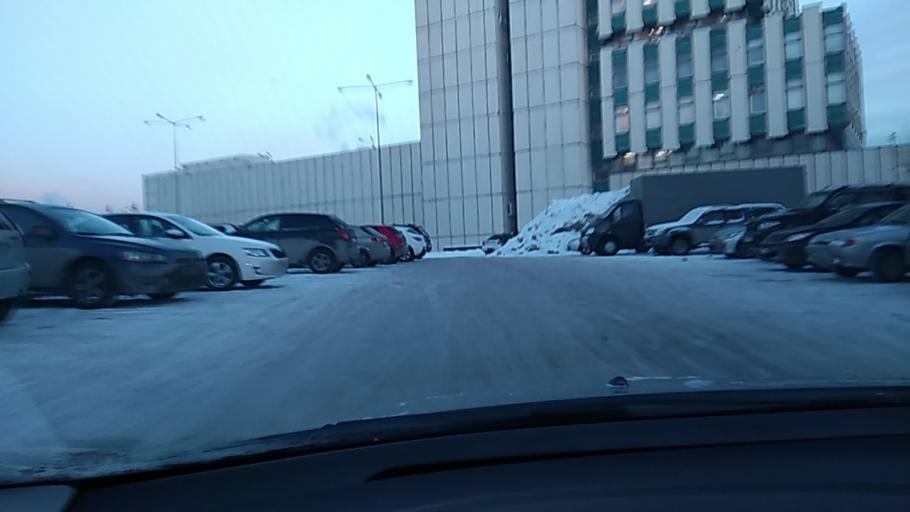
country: RU
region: Sverdlovsk
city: Yekaterinburg
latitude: 56.8213
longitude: 60.6402
